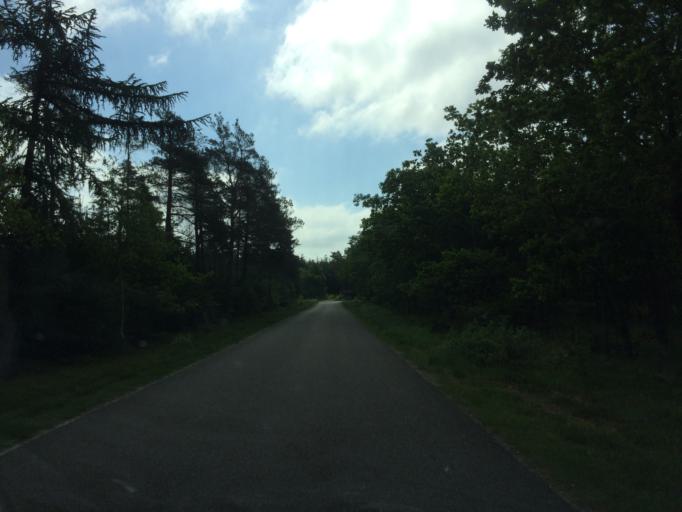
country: DK
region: Central Jutland
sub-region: Holstebro Kommune
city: Ulfborg
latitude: 56.2174
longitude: 8.4557
